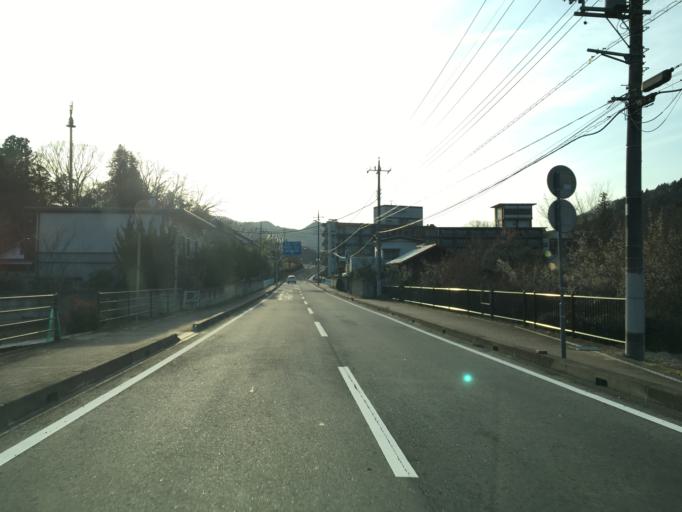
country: JP
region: Ibaraki
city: Daigo
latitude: 36.7592
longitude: 140.3934
